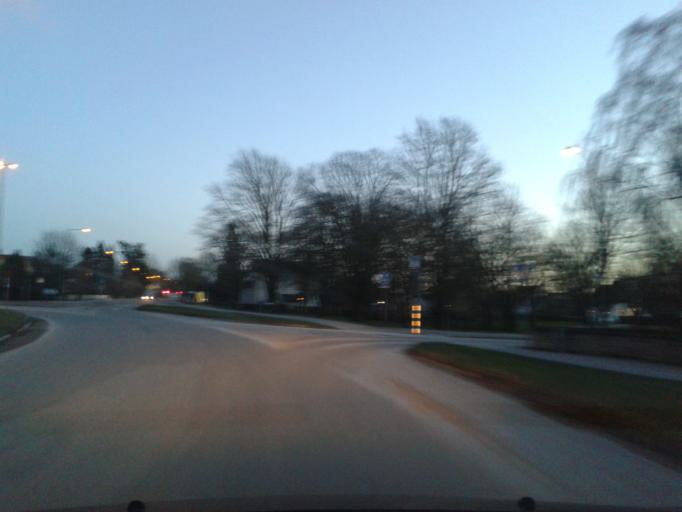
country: SE
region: Gotland
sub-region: Gotland
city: Visby
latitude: 57.6350
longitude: 18.3071
